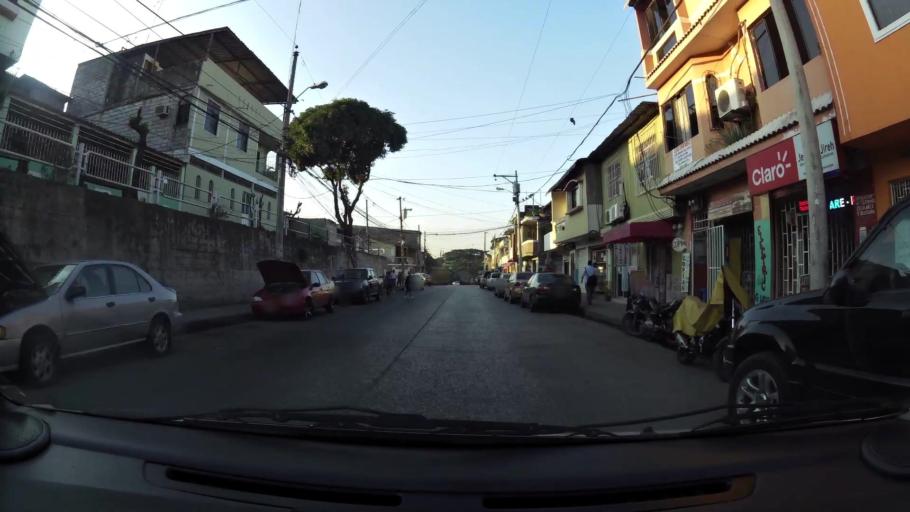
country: EC
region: Guayas
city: Guayaquil
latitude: -2.1450
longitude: -79.9189
